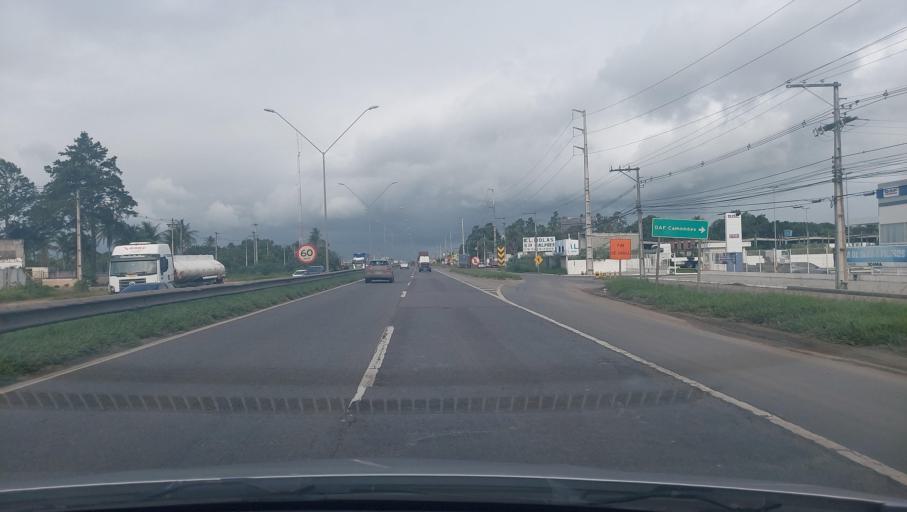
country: BR
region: Bahia
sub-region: Feira De Santana
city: Feira de Santana
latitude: -12.3164
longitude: -38.8773
